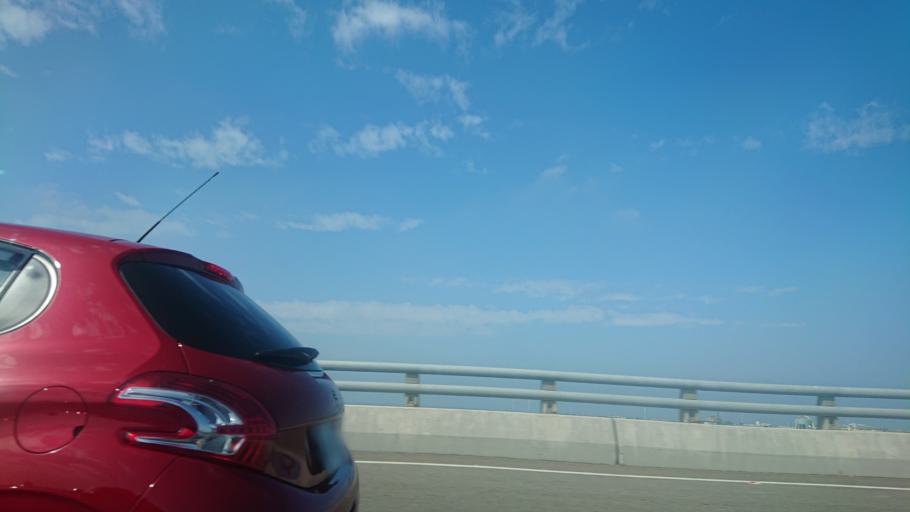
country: TW
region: Taiwan
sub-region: Changhua
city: Chang-hua
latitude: 24.0521
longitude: 120.4054
